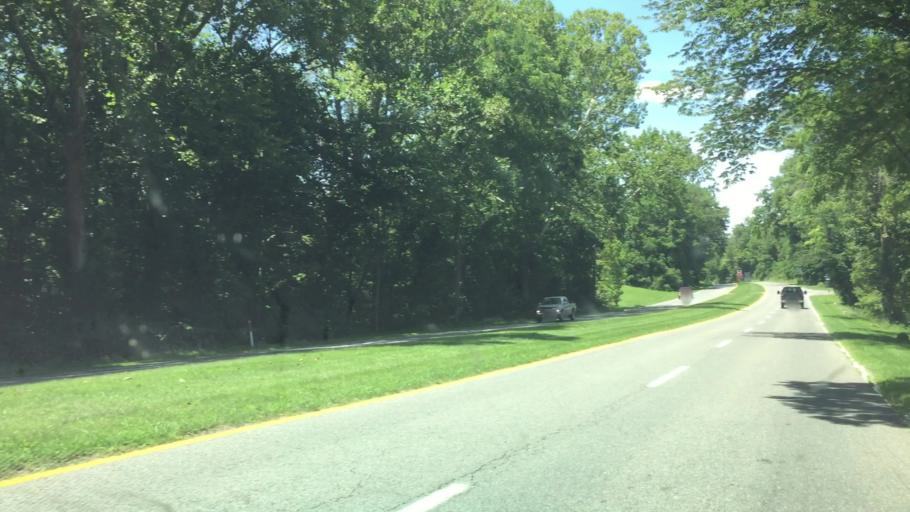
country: US
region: Virginia
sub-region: Pulaski County
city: Pulaski
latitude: 36.9500
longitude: -80.9031
